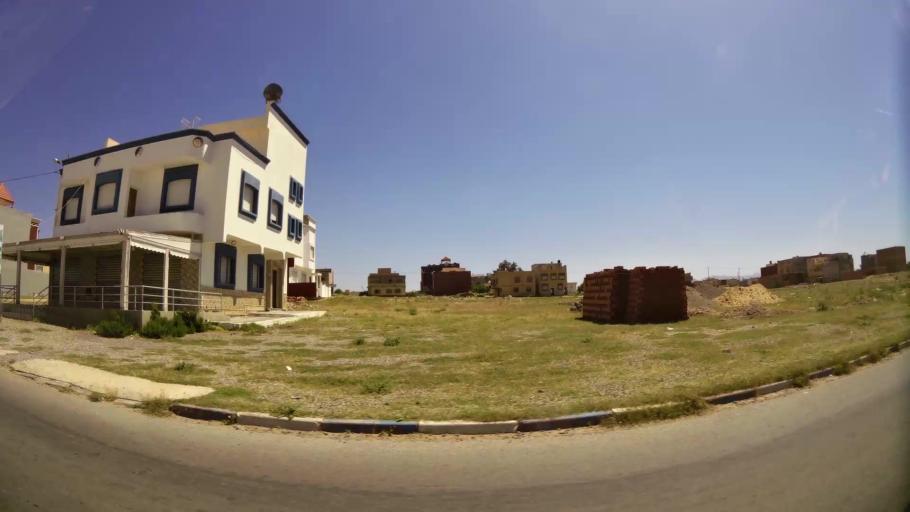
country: MA
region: Oriental
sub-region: Berkane-Taourirt
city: Madagh
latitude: 35.1351
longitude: -2.4088
